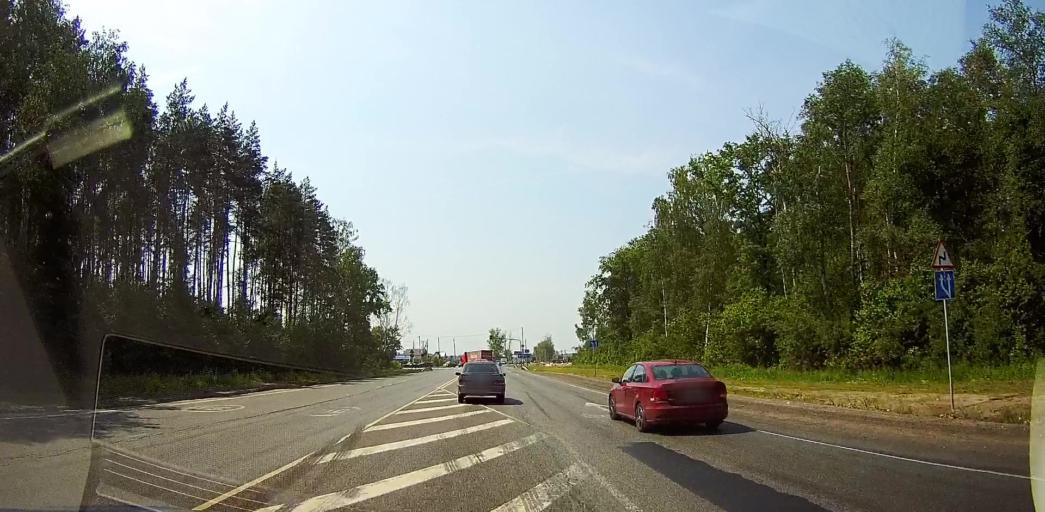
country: RU
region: Moskovskaya
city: Bronnitsy
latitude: 55.3924
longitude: 38.2064
